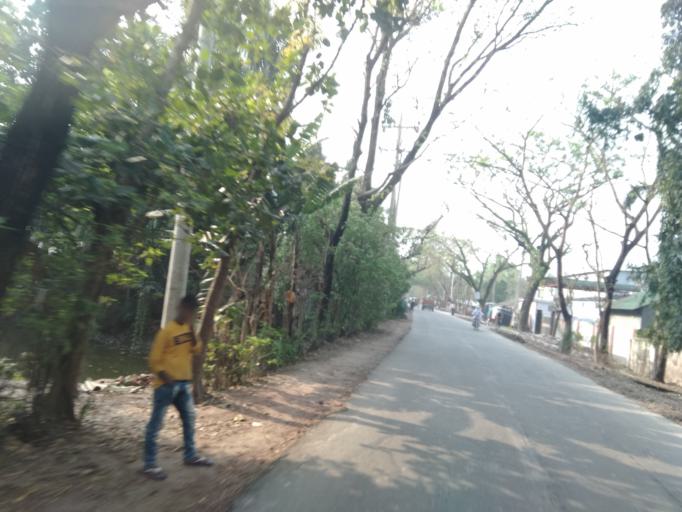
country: IN
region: West Bengal
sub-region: North 24 Parganas
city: Taki
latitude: 22.3273
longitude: 89.1054
